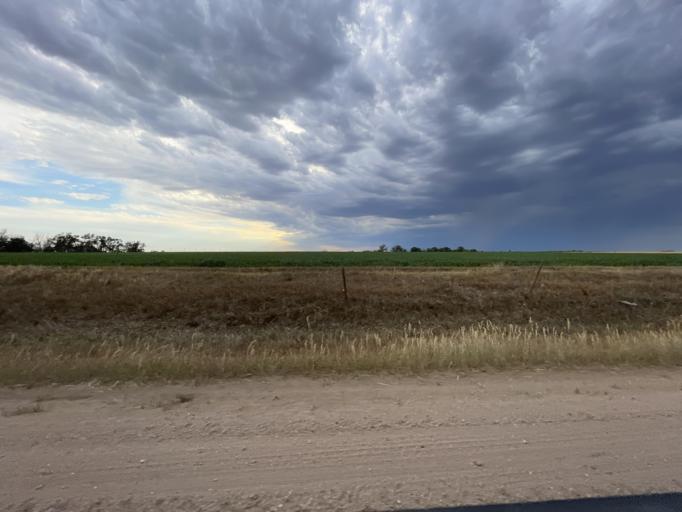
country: US
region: Nebraska
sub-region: Red Willow County
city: McCook
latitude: 40.2531
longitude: -100.7601
